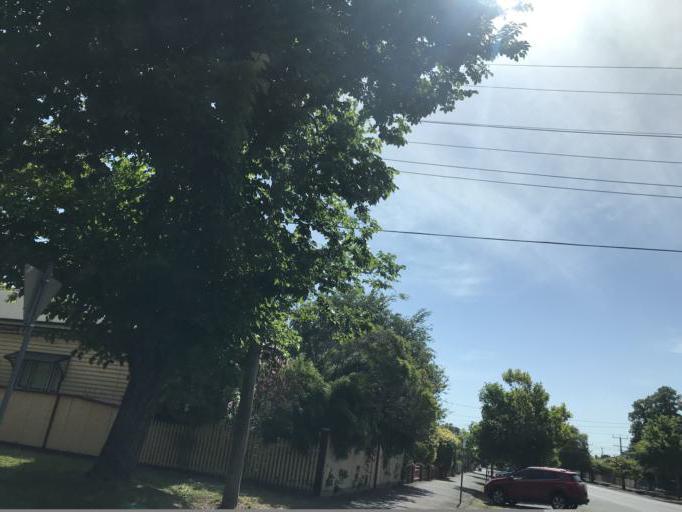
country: AU
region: Victoria
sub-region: Ballarat North
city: Ballarat Central
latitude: -37.5585
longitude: 143.8448
